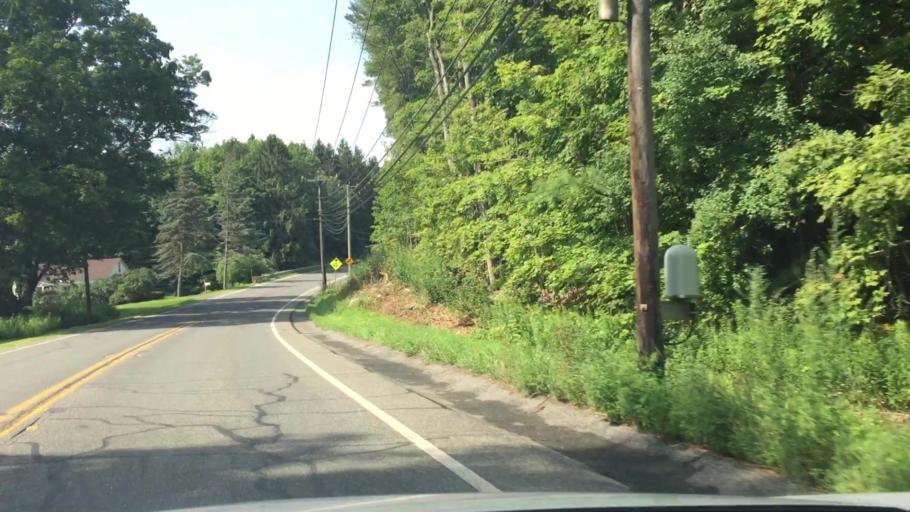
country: US
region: Massachusetts
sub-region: Berkshire County
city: Richmond
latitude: 42.4083
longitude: -73.3513
